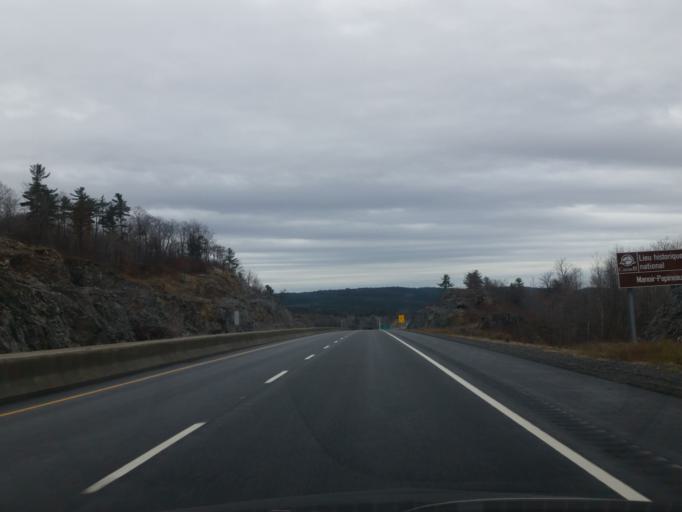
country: CA
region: Quebec
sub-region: Outaouais
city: Papineauville
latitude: 45.6729
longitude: -74.9569
